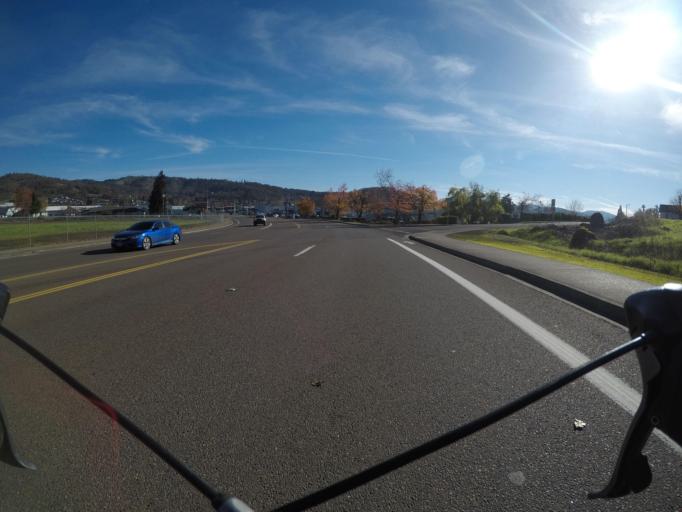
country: US
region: Oregon
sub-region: Douglas County
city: Roseburg
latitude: 43.2308
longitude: -123.3559
